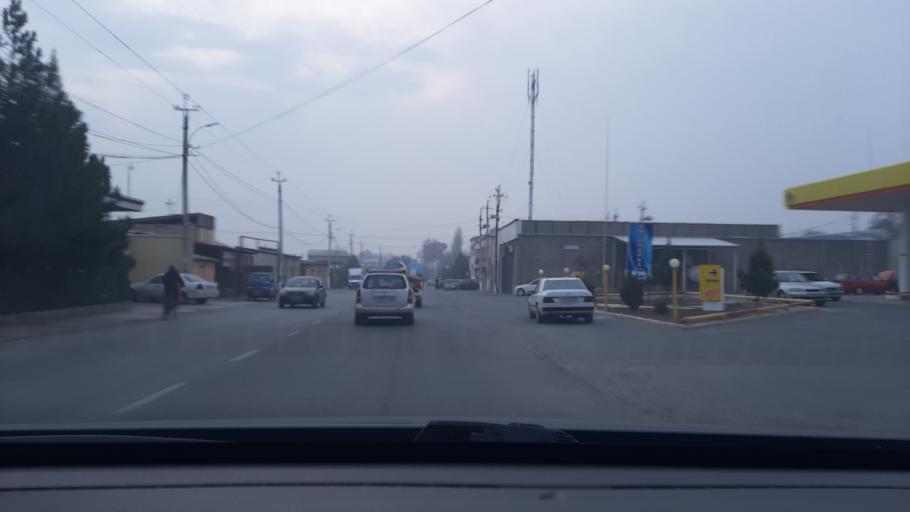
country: TJ
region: Viloyati Sughd
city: Khujand
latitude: 40.2621
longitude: 69.6004
